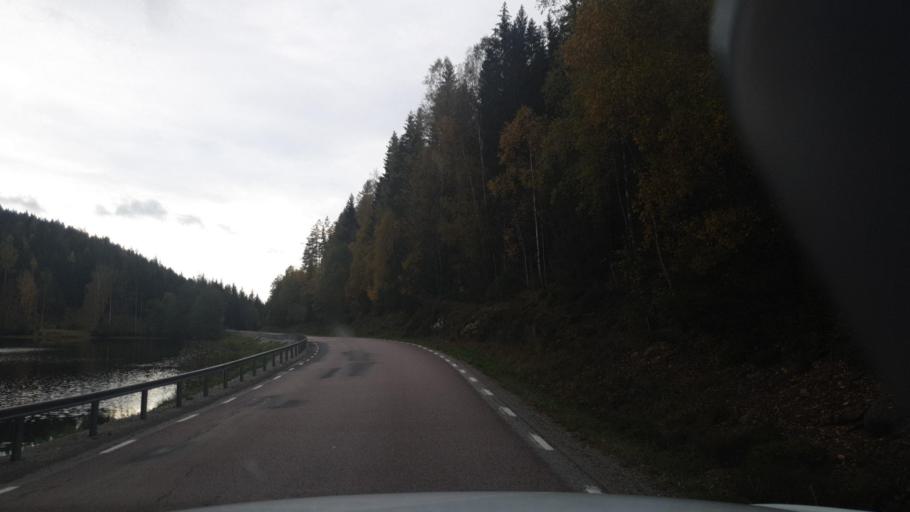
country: SE
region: Vaermland
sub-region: Arvika Kommun
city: Arvika
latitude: 59.7009
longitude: 12.7912
